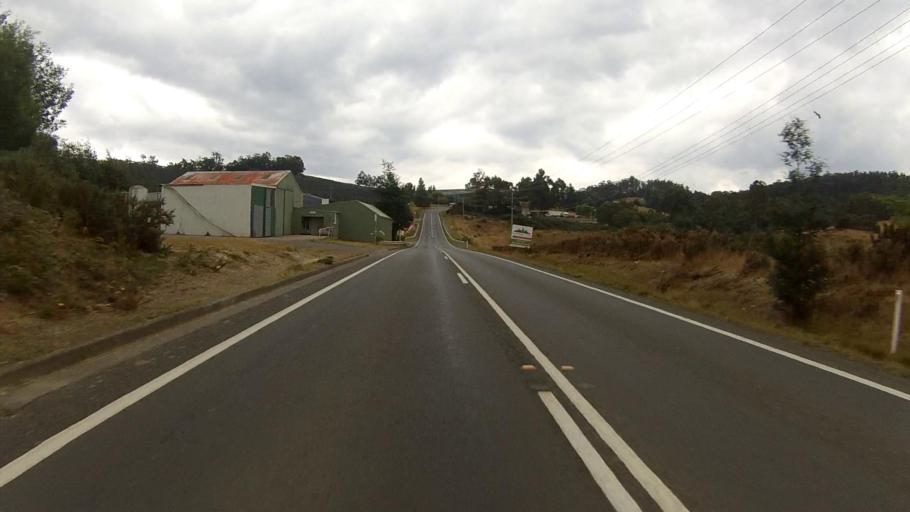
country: AU
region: Tasmania
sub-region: Huon Valley
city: Cygnet
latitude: -43.1326
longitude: 147.0500
